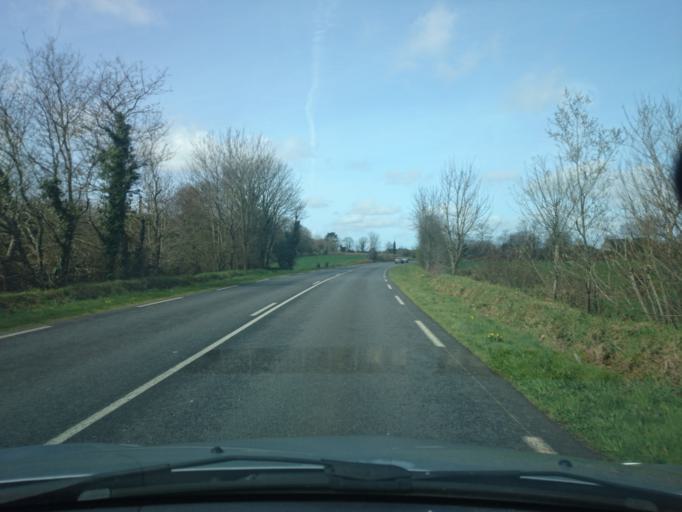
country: FR
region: Brittany
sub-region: Departement du Finistere
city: Gouesnou
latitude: 48.4411
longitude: -4.4481
